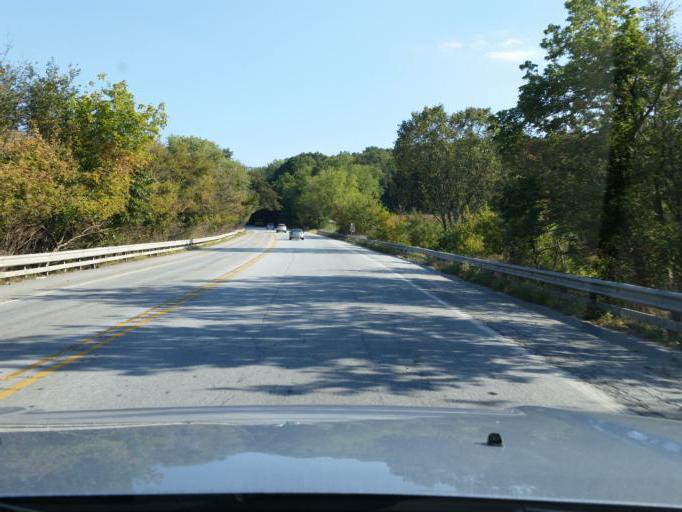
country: US
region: Pennsylvania
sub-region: Chester County
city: Atglen
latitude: 39.9428
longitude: -75.9660
